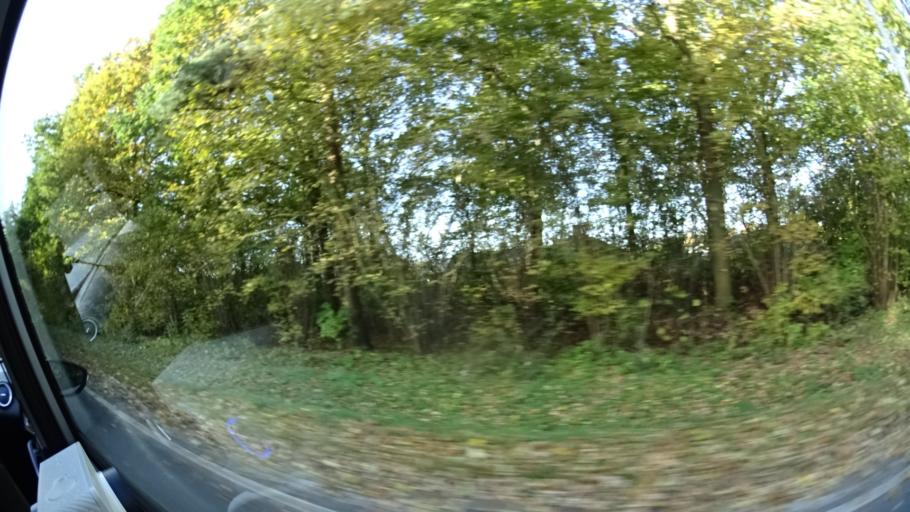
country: DK
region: South Denmark
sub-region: Odense Kommune
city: Hojby
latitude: 55.3373
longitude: 10.4377
